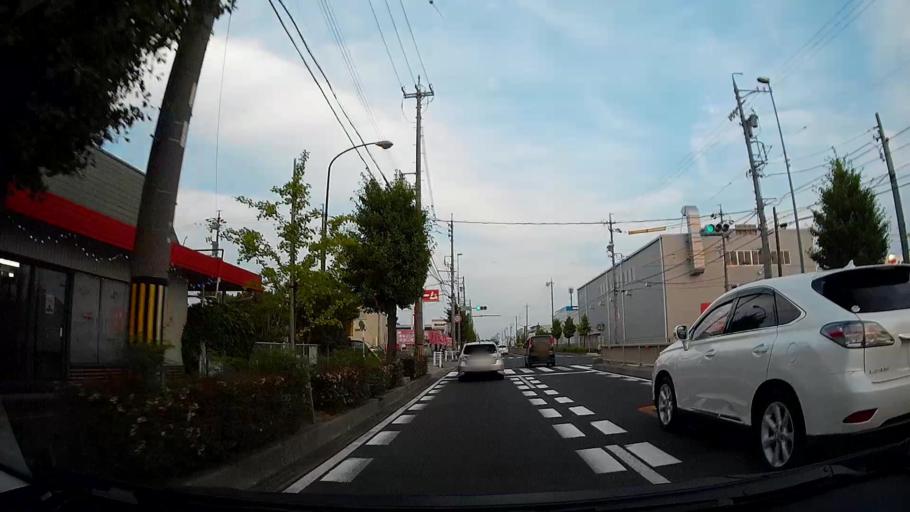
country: JP
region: Aichi
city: Toyohashi
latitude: 34.7838
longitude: 137.3799
